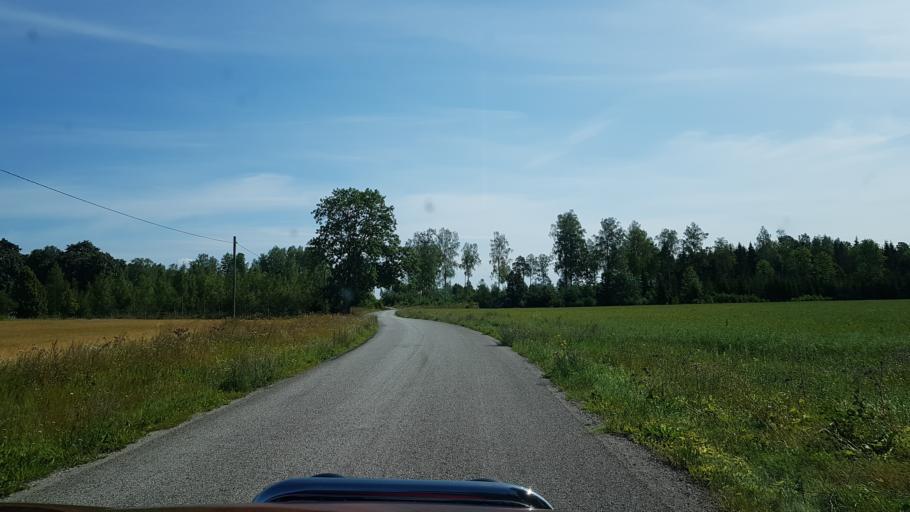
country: EE
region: Jaervamaa
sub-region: Jaerva-Jaani vald
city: Jarva-Jaani
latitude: 59.1181
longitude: 25.6950
